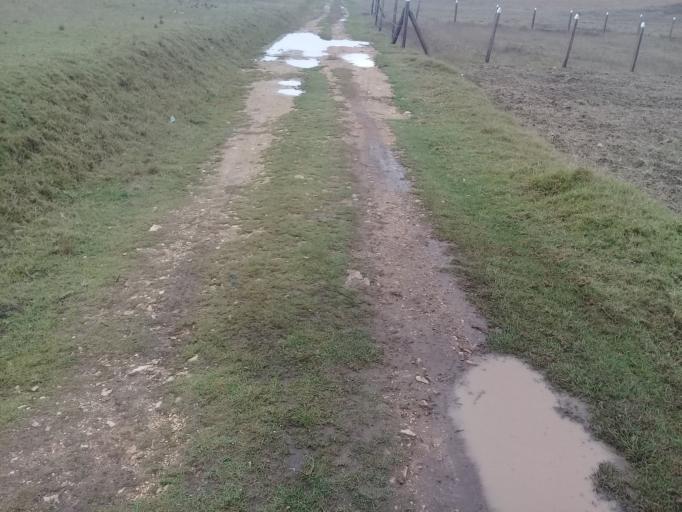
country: CO
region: Boyaca
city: Siachoque
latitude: 5.5627
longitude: -73.2779
